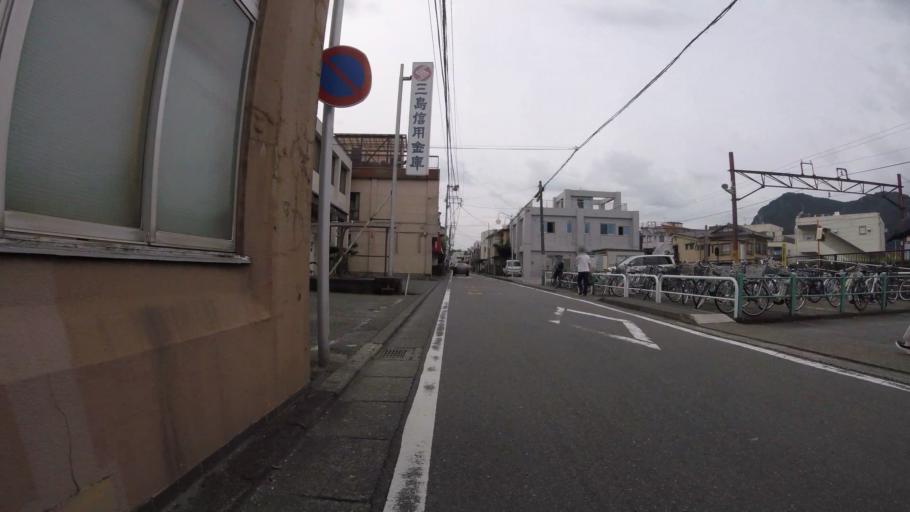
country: JP
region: Shizuoka
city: Mishima
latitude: 35.0147
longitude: 138.9460
